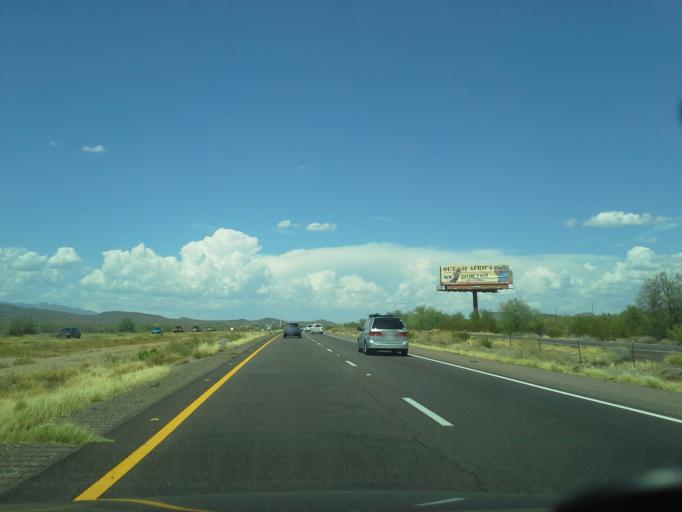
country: US
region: Arizona
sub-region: Maricopa County
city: Anthem
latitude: 33.8877
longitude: -112.1474
